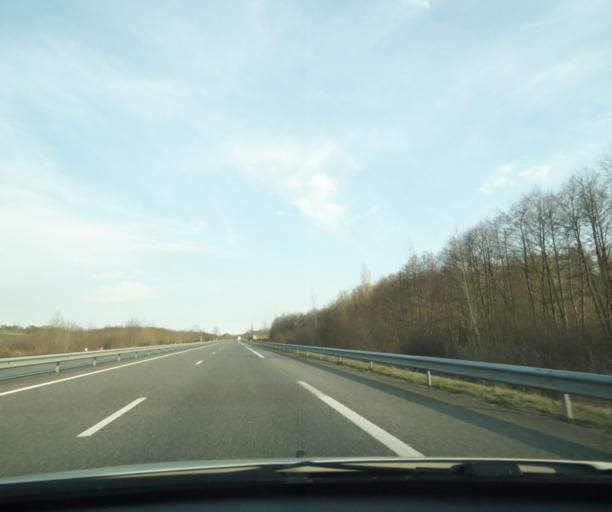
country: FR
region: Midi-Pyrenees
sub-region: Departement de la Haute-Garonne
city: Aurignac
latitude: 43.1315
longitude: 0.8443
